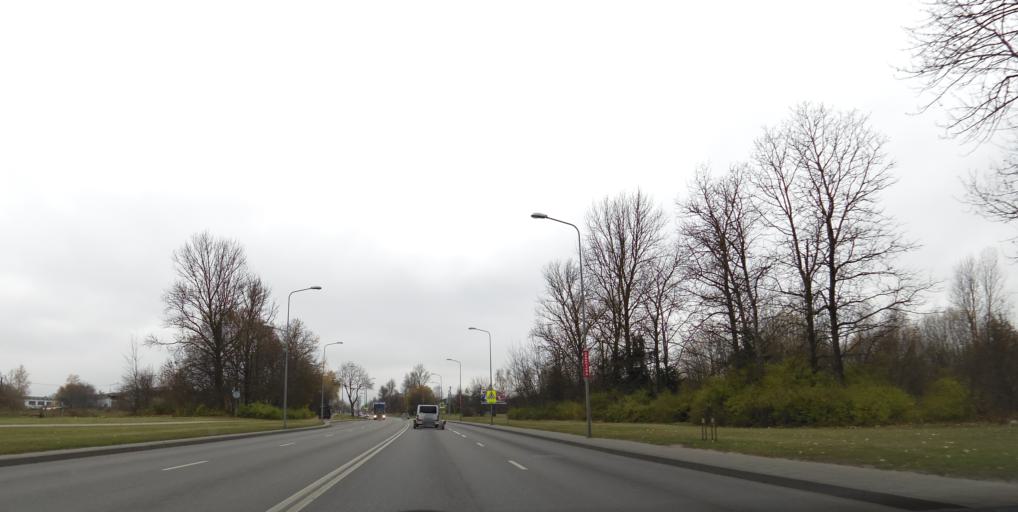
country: LT
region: Vilnius County
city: Vilkpede
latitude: 54.6504
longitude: 25.2692
